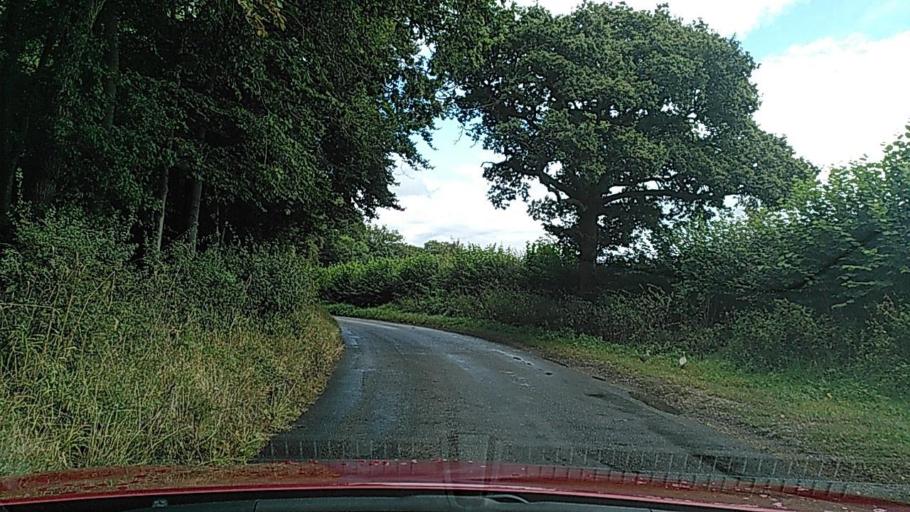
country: GB
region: England
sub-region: Oxfordshire
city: Sonning Common
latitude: 51.4979
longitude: -0.9456
